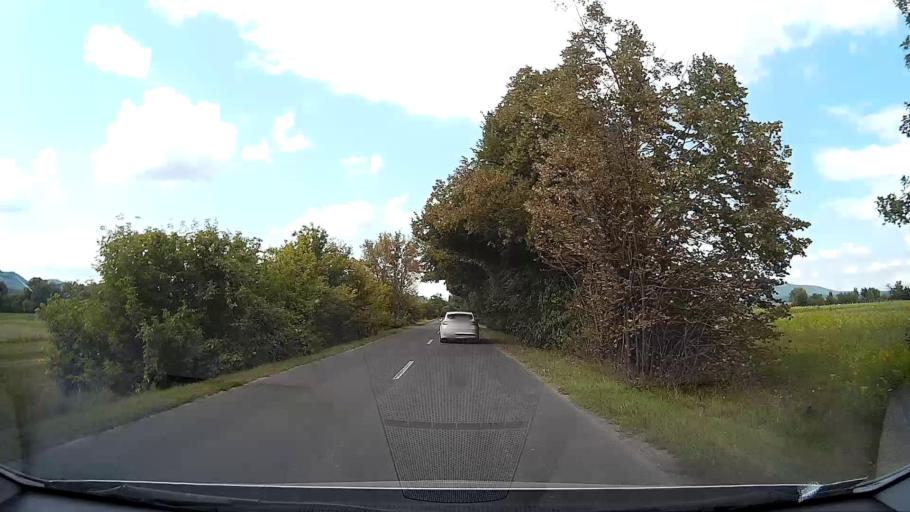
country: HU
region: Pest
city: Tahitotfalu
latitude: 47.7361
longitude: 19.1025
